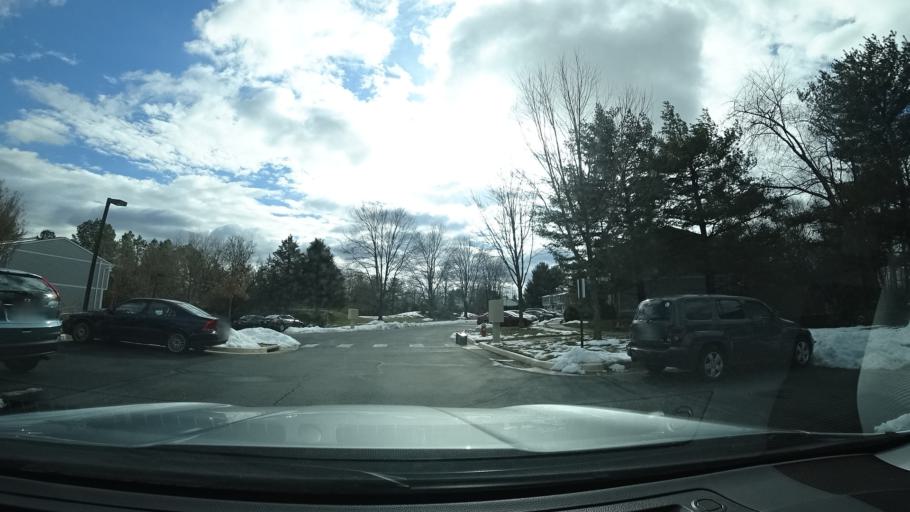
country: US
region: Virginia
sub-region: Fairfax County
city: Reston
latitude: 38.9732
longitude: -77.3633
